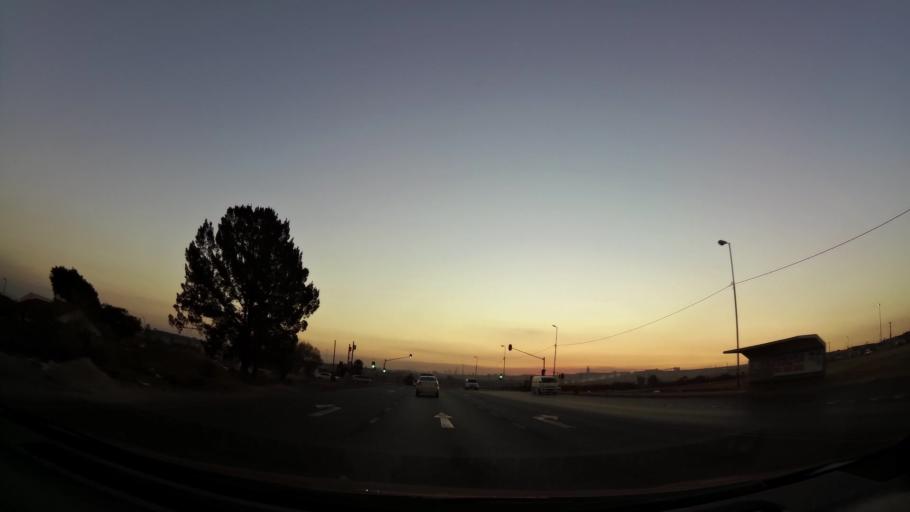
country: ZA
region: Gauteng
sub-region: City of Johannesburg Metropolitan Municipality
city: Soweto
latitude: -26.2310
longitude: 27.8183
